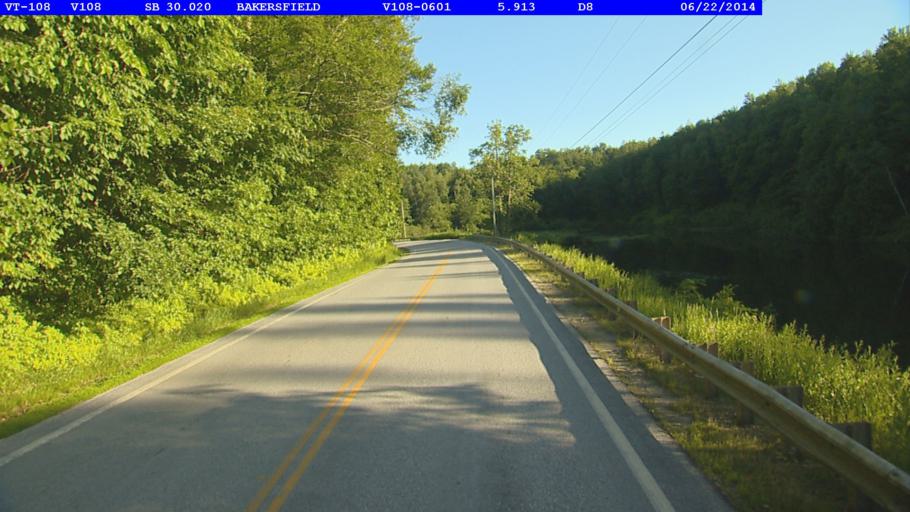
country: US
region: Vermont
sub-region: Franklin County
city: Enosburg Falls
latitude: 44.8114
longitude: -72.7902
